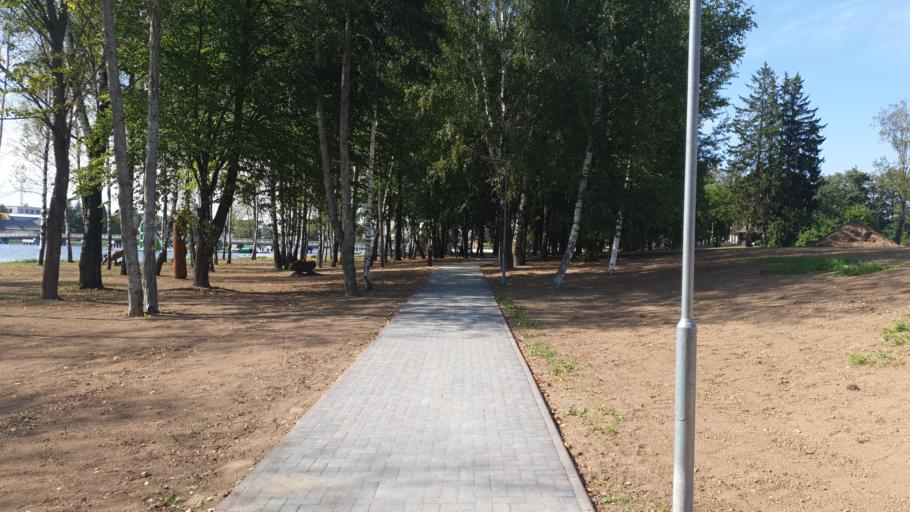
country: LT
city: Sirvintos
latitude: 55.0424
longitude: 24.9629
